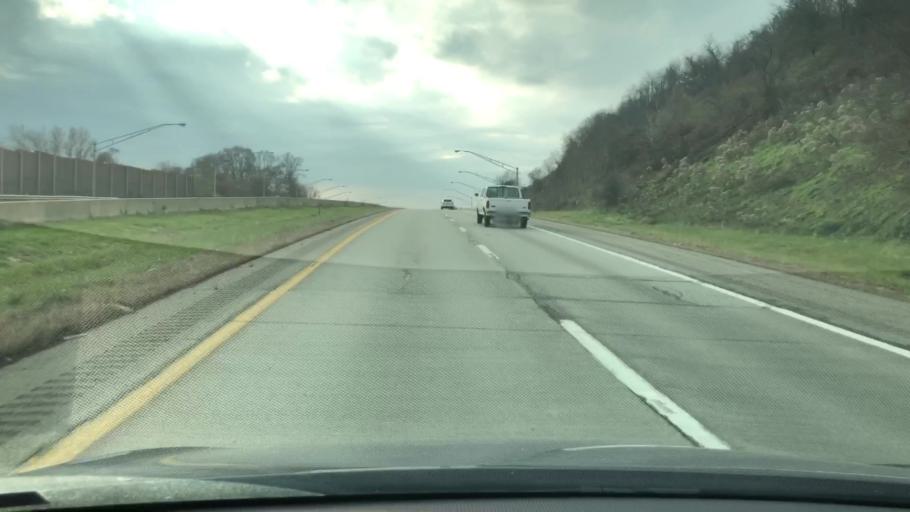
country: US
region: Pennsylvania
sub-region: Allegheny County
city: Cheswick
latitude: 40.5576
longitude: -79.8058
